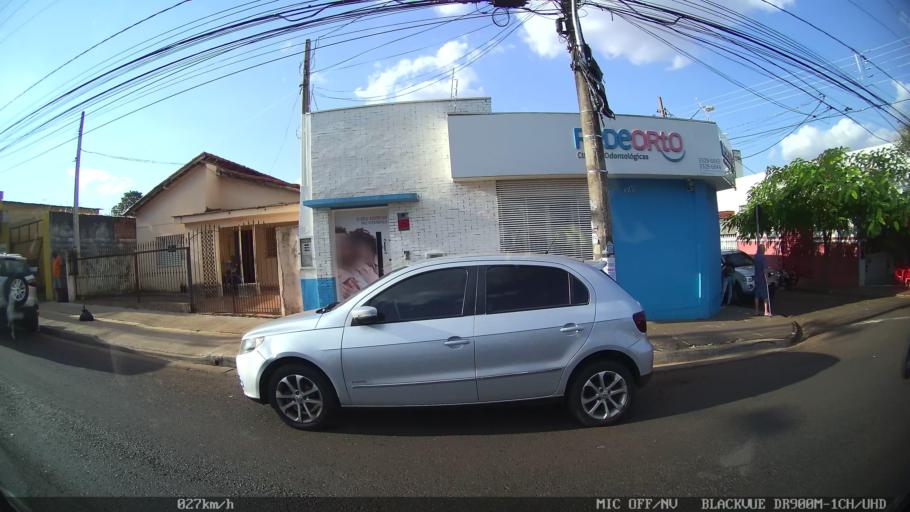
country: BR
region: Sao Paulo
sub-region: Ribeirao Preto
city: Ribeirao Preto
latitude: -21.1521
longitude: -47.8242
